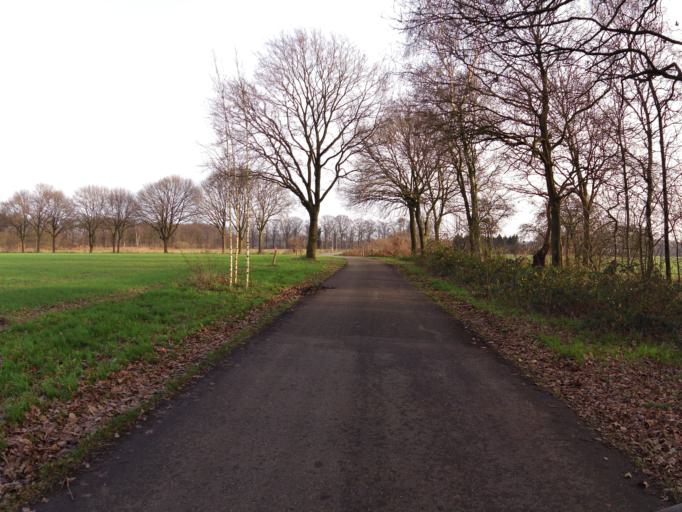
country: NL
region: North Brabant
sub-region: Gemeente Vught
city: Vught
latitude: 51.6623
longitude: 5.3090
